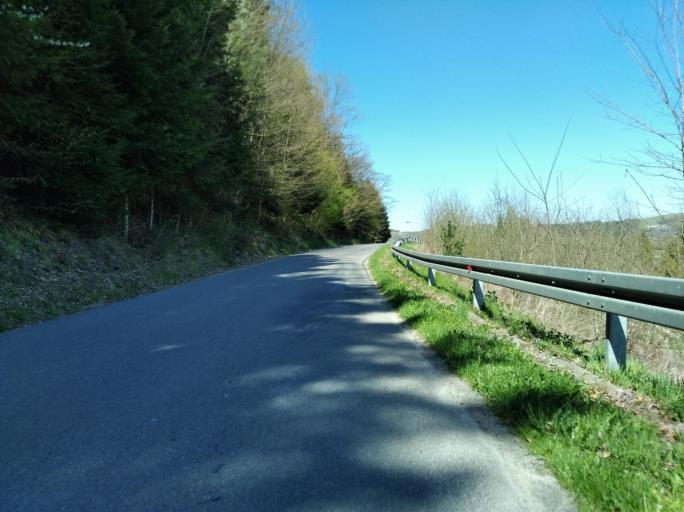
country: PL
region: Subcarpathian Voivodeship
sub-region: Powiat brzozowski
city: Dydnia
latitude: 49.6921
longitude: 22.2050
